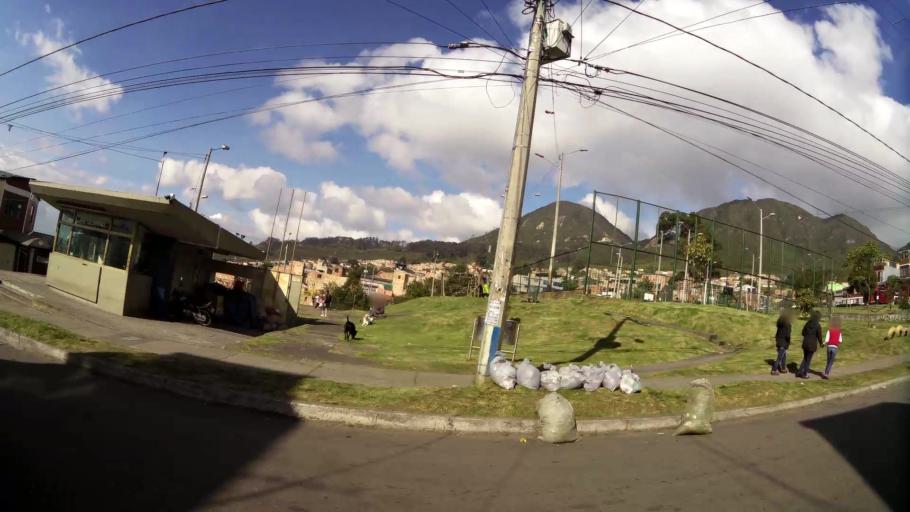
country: CO
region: Bogota D.C.
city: Bogota
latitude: 4.5369
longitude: -74.0861
